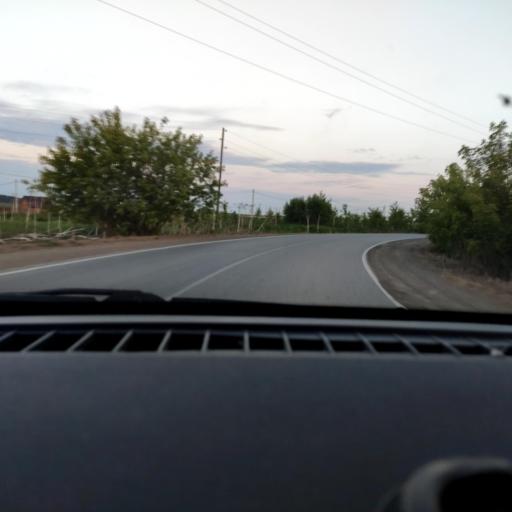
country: RU
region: Perm
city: Kukushtan
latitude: 57.6373
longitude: 56.5101
